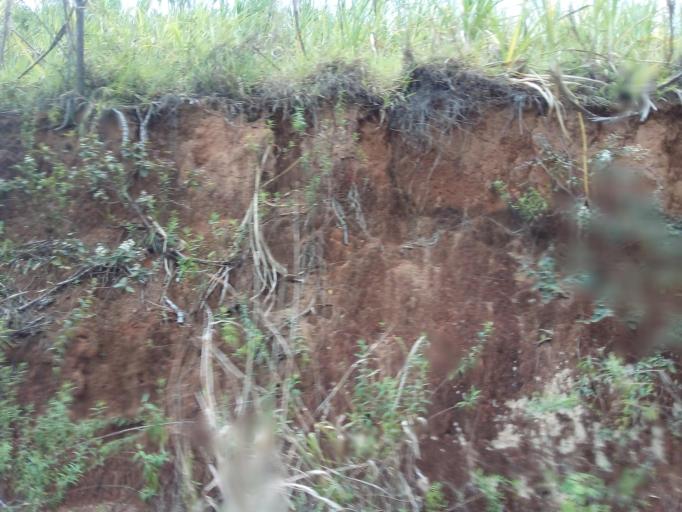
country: BR
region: Espirito Santo
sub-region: Ibiracu
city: Ibiracu
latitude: -19.7954
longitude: -40.3692
